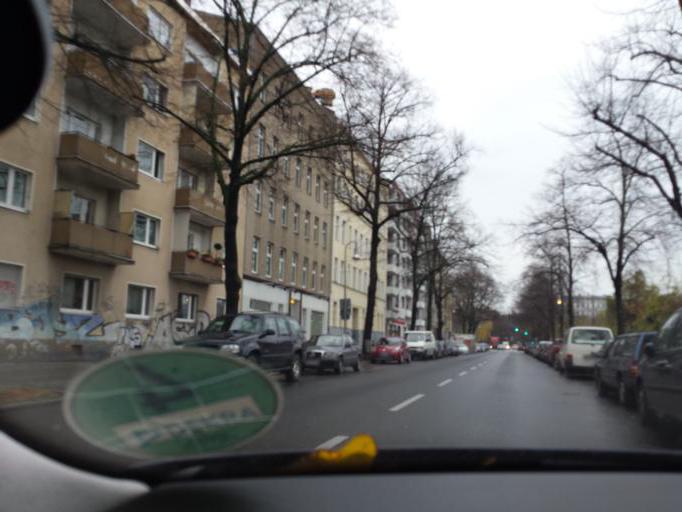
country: DE
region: Berlin
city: Bezirk Kreuzberg
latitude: 52.4942
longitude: 13.3796
